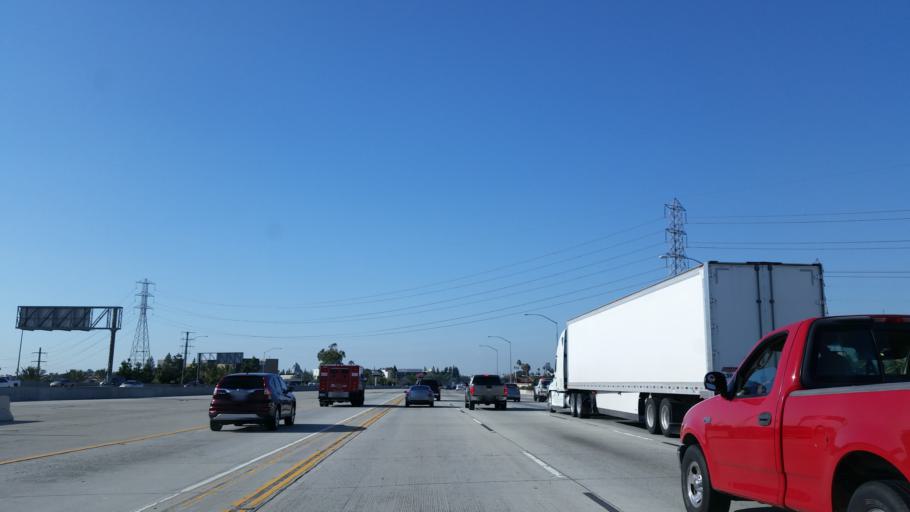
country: US
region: California
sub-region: Orange County
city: Anaheim
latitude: 33.8057
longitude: -117.9047
